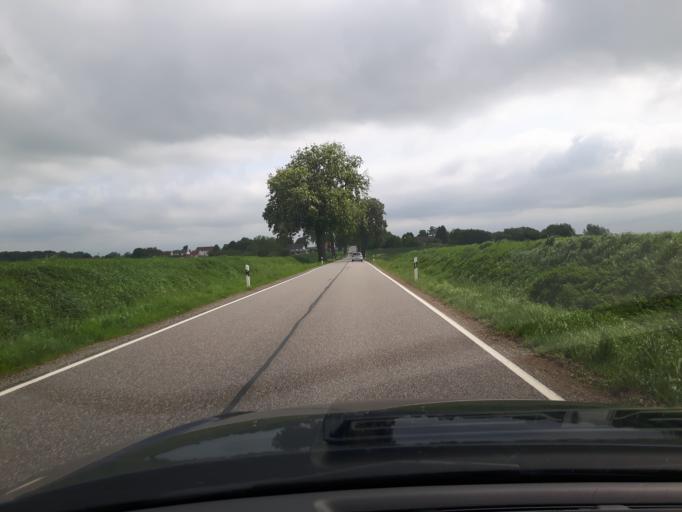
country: DE
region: Mecklenburg-Vorpommern
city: Gross Wokern
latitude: 53.6617
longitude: 12.5156
